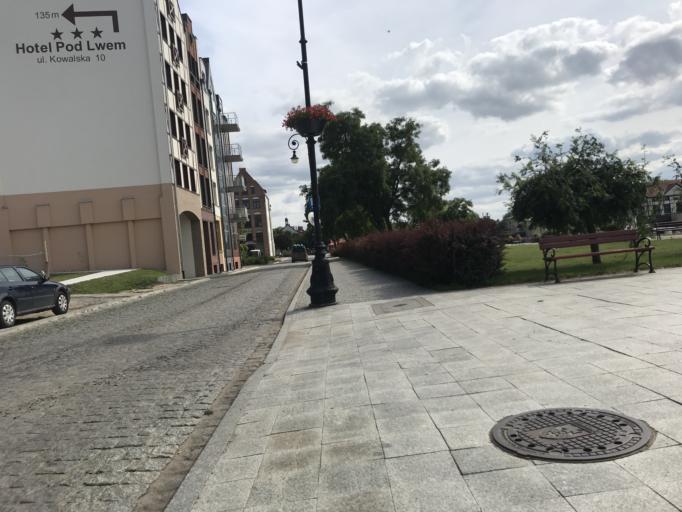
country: PL
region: Warmian-Masurian Voivodeship
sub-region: Powiat elblaski
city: Elblag
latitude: 54.1593
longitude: 19.3929
